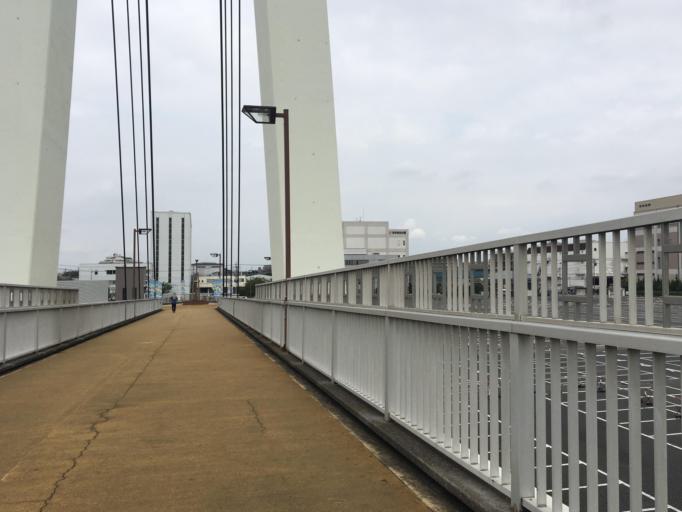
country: JP
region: Saitama
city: Shimotoda
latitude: 35.8042
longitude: 139.6607
